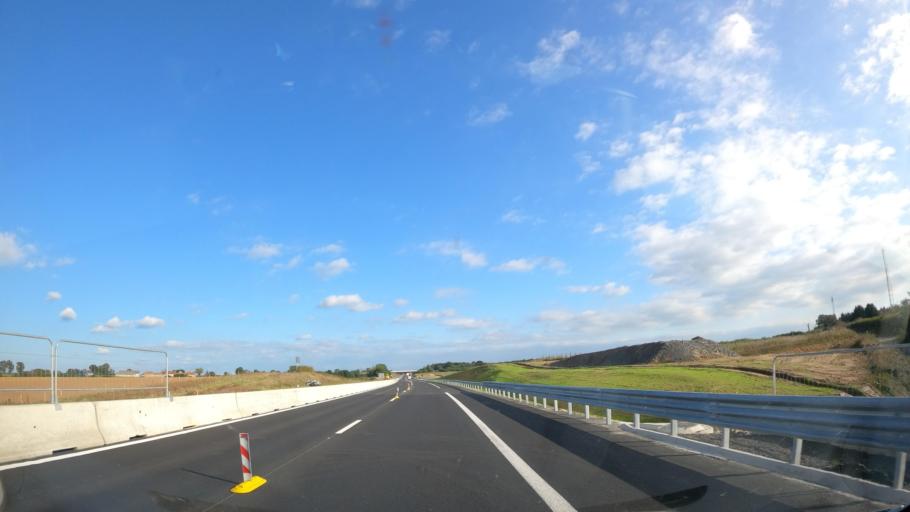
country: FR
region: Auvergne
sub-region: Departement de l'Allier
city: Diou
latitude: 46.5174
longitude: 3.7404
